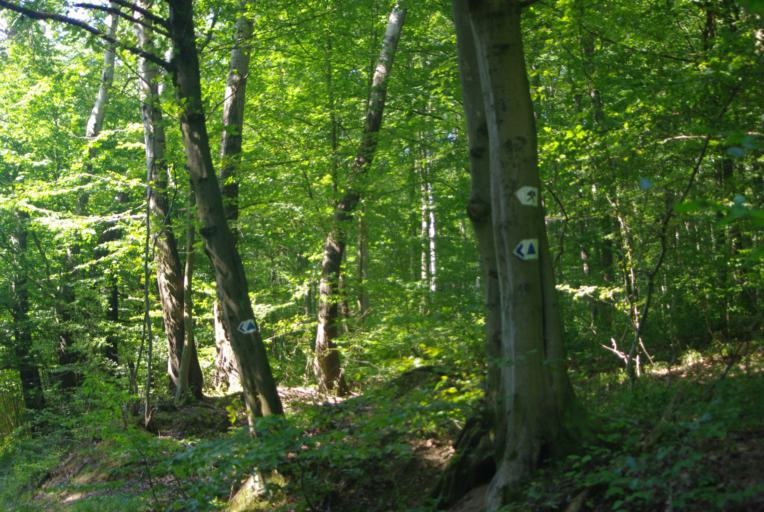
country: HU
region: Baranya
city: Pellerd
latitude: 46.1159
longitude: 18.1283
